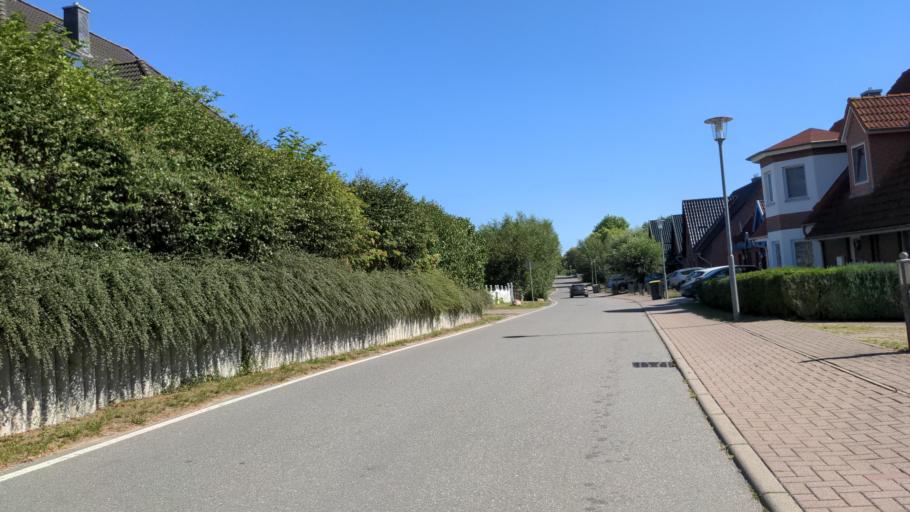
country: DE
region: Mecklenburg-Vorpommern
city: Ostseebad Boltenhagen
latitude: 53.9935
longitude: 11.1826
